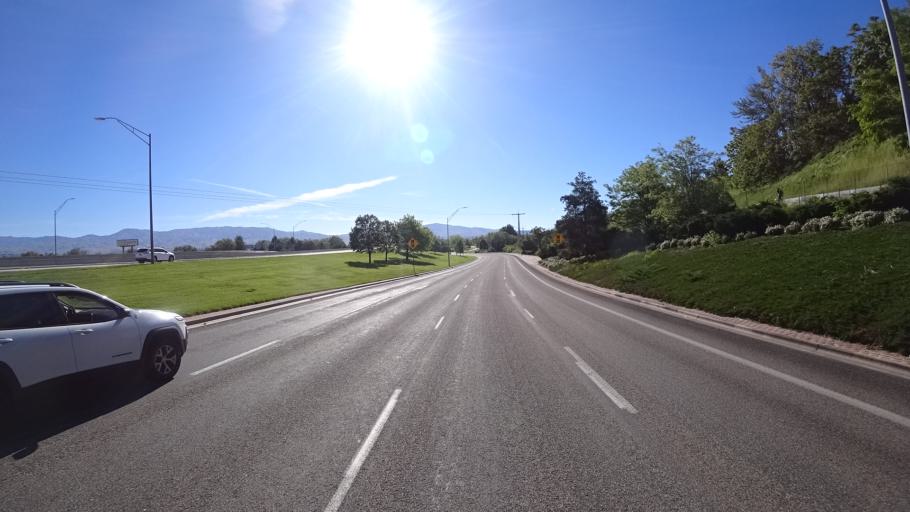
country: US
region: Idaho
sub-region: Ada County
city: Garden City
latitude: 43.6184
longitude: -116.2369
